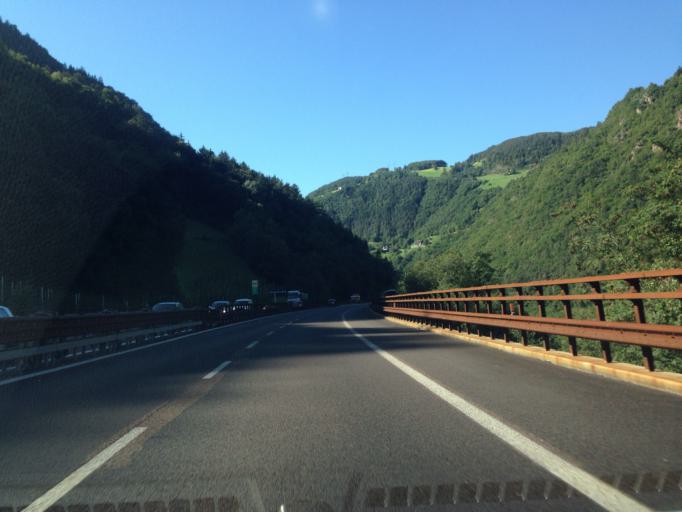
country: IT
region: Trentino-Alto Adige
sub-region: Bolzano
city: Ponte Gardena
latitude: 46.5670
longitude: 11.5210
